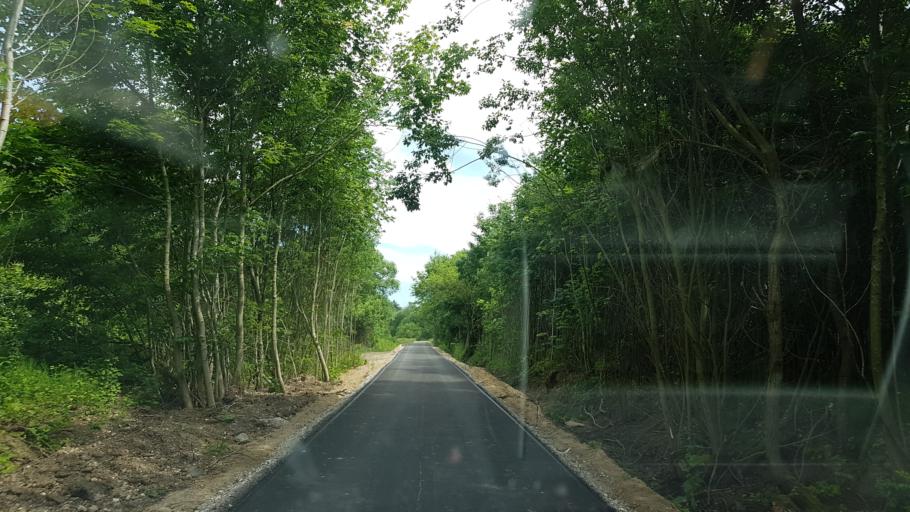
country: PL
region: Pomeranian Voivodeship
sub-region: Powiat slupski
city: Ustka
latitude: 54.5148
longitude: 16.7379
